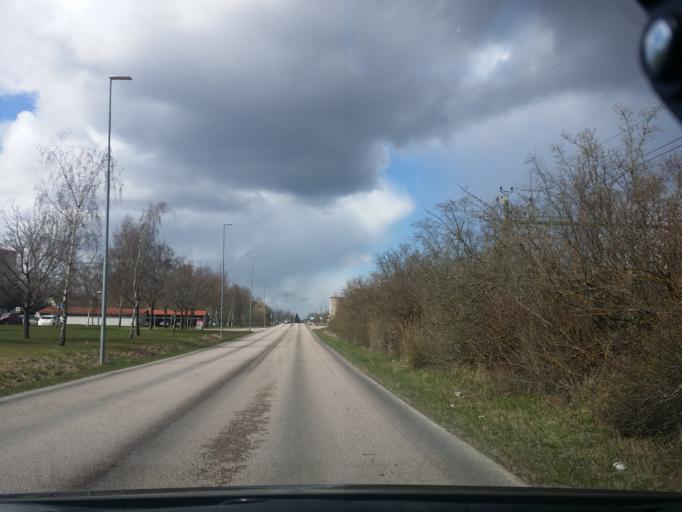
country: SE
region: Vaestmanland
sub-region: Sala Kommun
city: Sala
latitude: 59.9271
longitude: 16.5995
